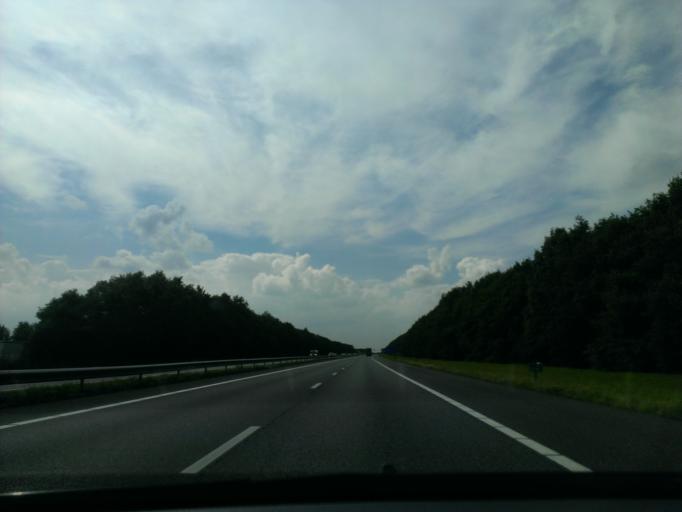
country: NL
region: Gelderland
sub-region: Gemeente Barneveld
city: Voorthuizen
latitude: 52.1695
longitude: 5.6085
